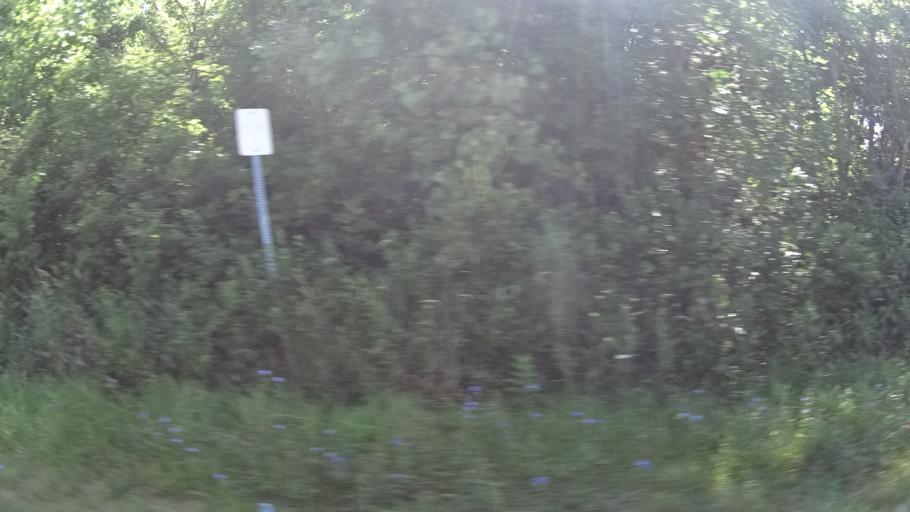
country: US
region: Ohio
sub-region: Huron County
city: Bellevue
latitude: 41.4097
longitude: -82.8467
